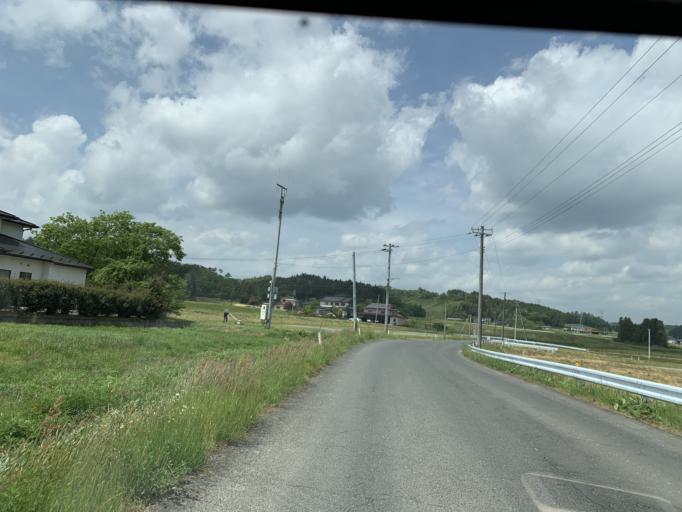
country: JP
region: Miyagi
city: Furukawa
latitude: 38.7666
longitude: 140.9478
